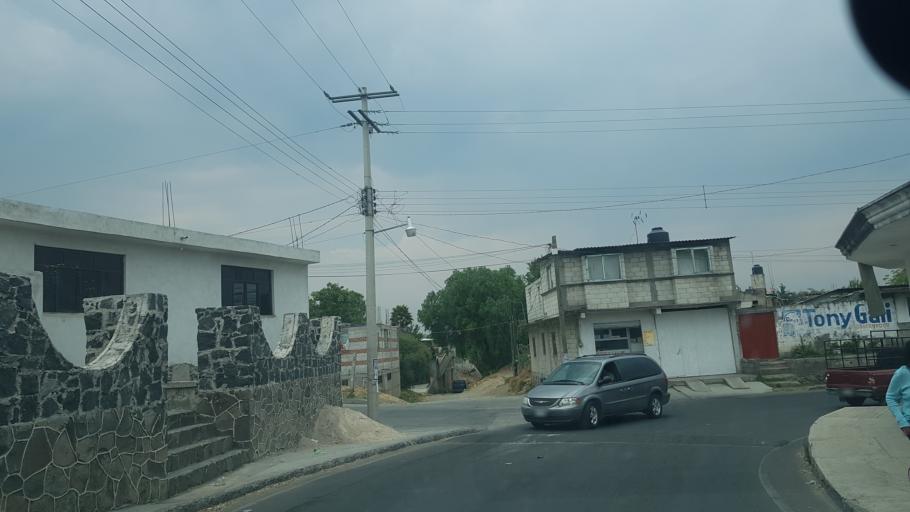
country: MX
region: Puebla
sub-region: Huejotzingo
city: San Mateo Capultitlan
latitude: 19.1979
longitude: -98.4402
